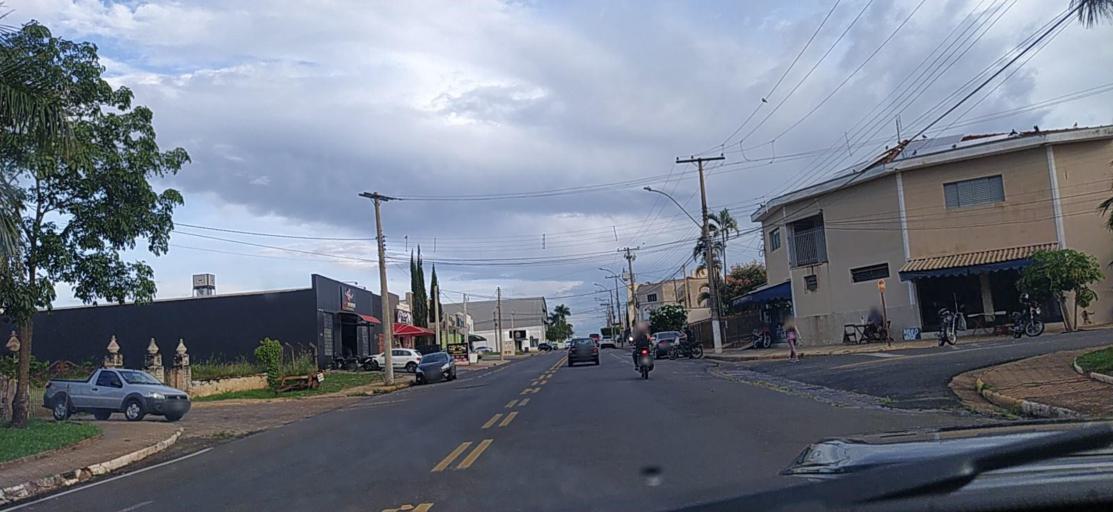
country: BR
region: Sao Paulo
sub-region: Pindorama
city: Pindorama
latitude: -21.1833
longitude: -48.9136
